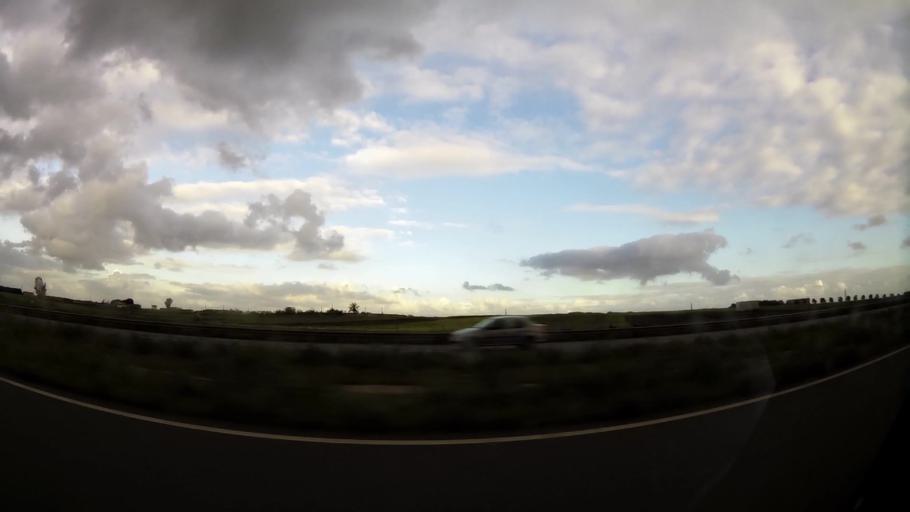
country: MA
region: Grand Casablanca
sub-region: Mediouna
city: Tit Mellil
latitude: 33.5746
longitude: -7.4553
